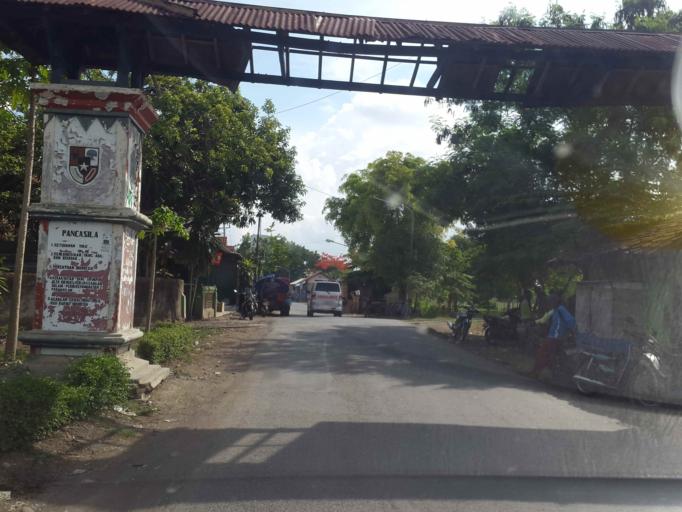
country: ID
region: Central Java
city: Pemalang
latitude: -6.9169
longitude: 109.3274
